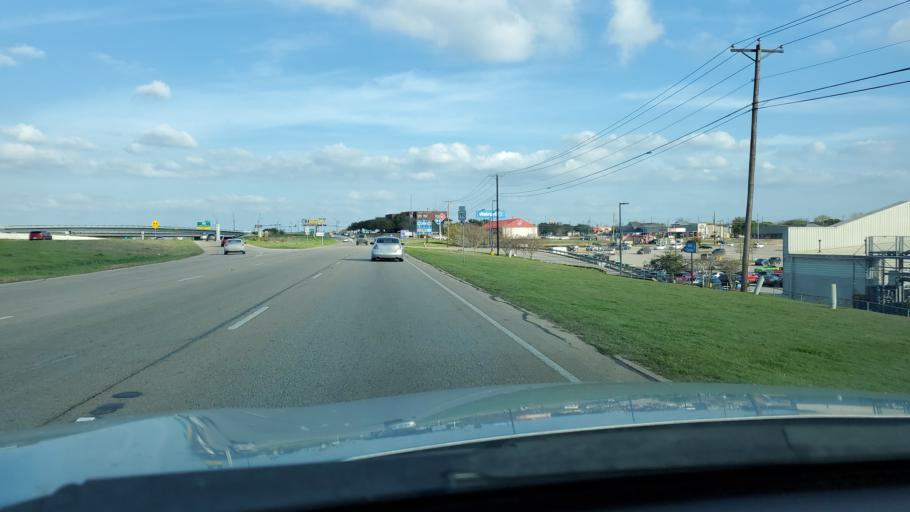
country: US
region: Texas
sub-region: Bell County
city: Harker Heights
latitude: 31.0712
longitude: -97.6739
